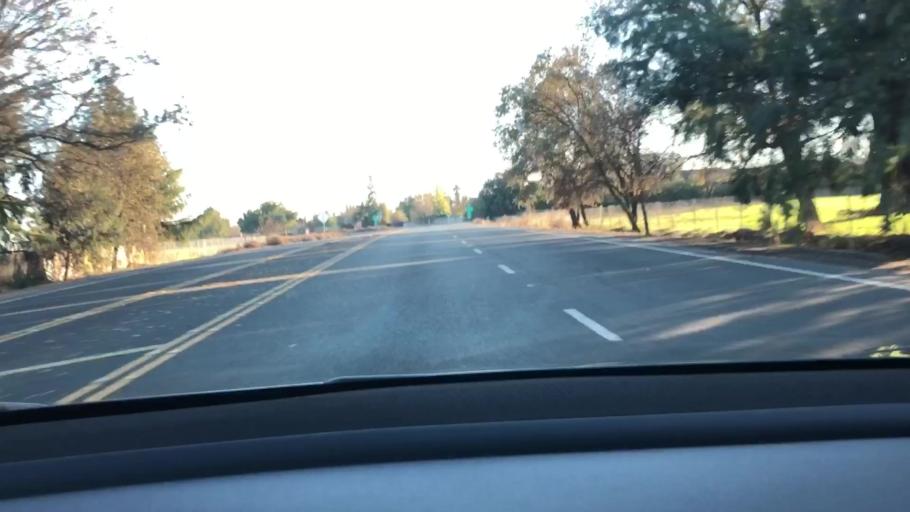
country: US
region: California
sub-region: Yolo County
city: Woodland
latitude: 38.6766
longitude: -121.7530
